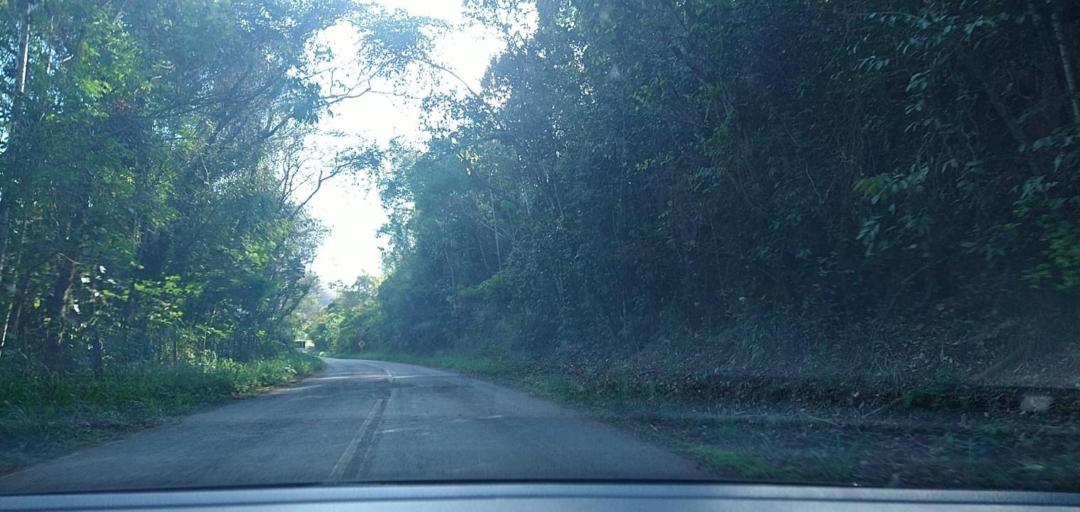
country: BR
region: Minas Gerais
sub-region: Alvinopolis
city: Alvinopolis
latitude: -20.1730
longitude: -42.9221
